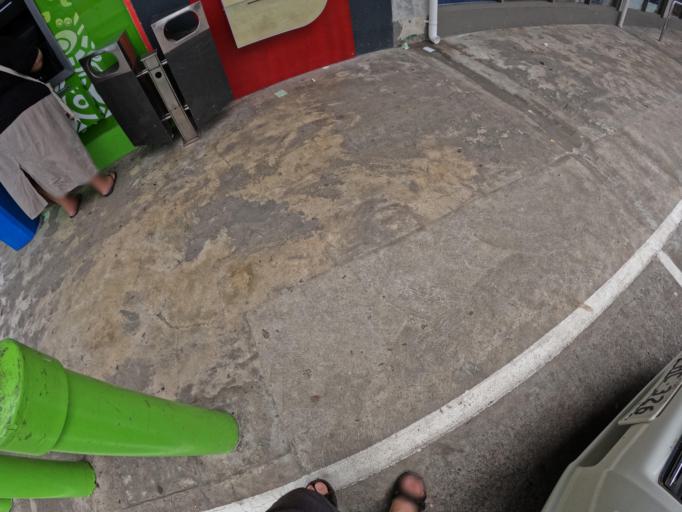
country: FJ
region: Central
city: Suva
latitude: -18.1145
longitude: 178.4383
